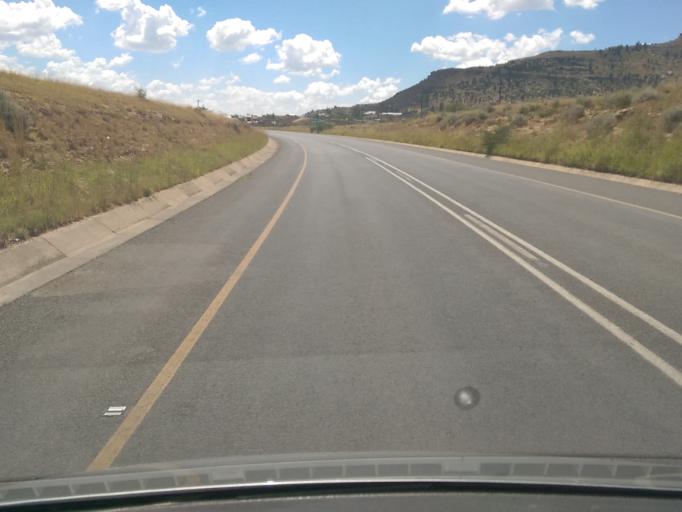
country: LS
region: Maseru
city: Maseru
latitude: -29.3682
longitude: 27.4735
